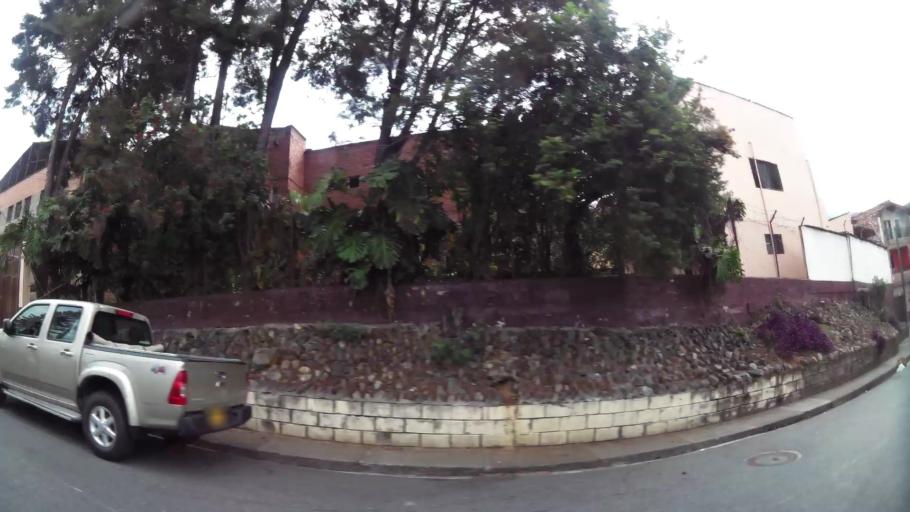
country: CO
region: Antioquia
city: Medellin
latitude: 6.2777
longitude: -75.5516
